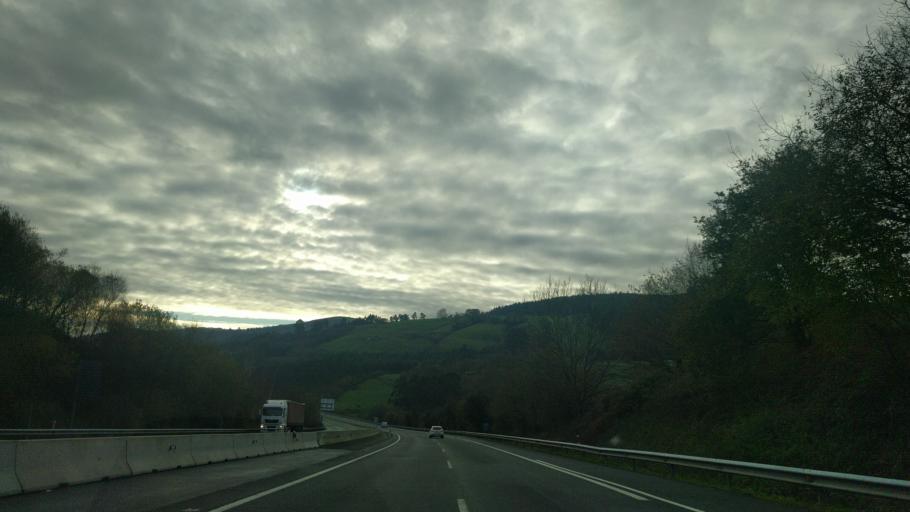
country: ES
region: Cantabria
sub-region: Provincia de Cantabria
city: Laredo
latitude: 43.3947
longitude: -3.3977
